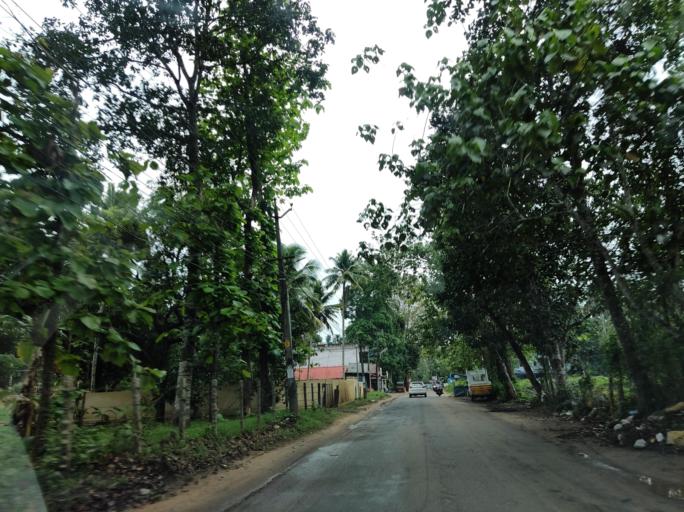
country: IN
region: Kerala
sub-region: Alappuzha
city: Mavelikara
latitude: 9.2424
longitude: 76.5283
